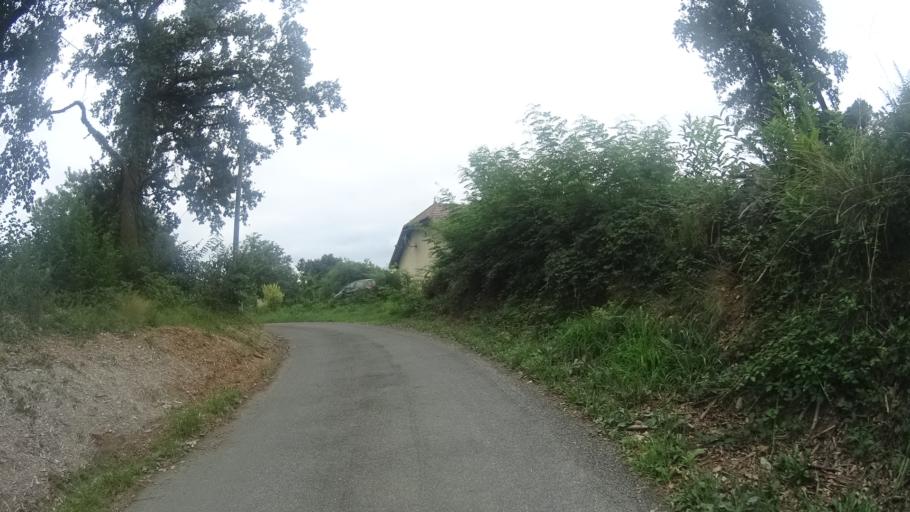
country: FR
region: Aquitaine
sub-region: Departement des Pyrenees-Atlantiques
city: Mont
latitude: 43.4861
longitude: -0.6870
